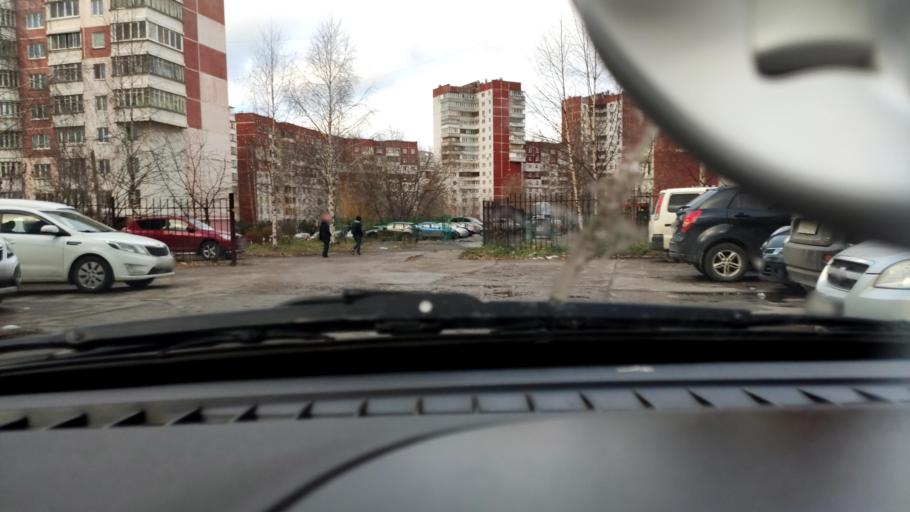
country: RU
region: Perm
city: Perm
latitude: 58.0042
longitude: 56.2993
